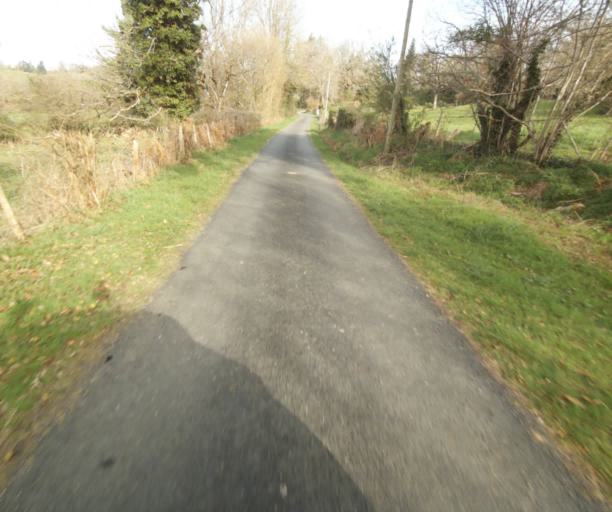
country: FR
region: Limousin
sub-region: Departement de la Correze
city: Chamboulive
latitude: 45.4197
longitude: 1.7643
